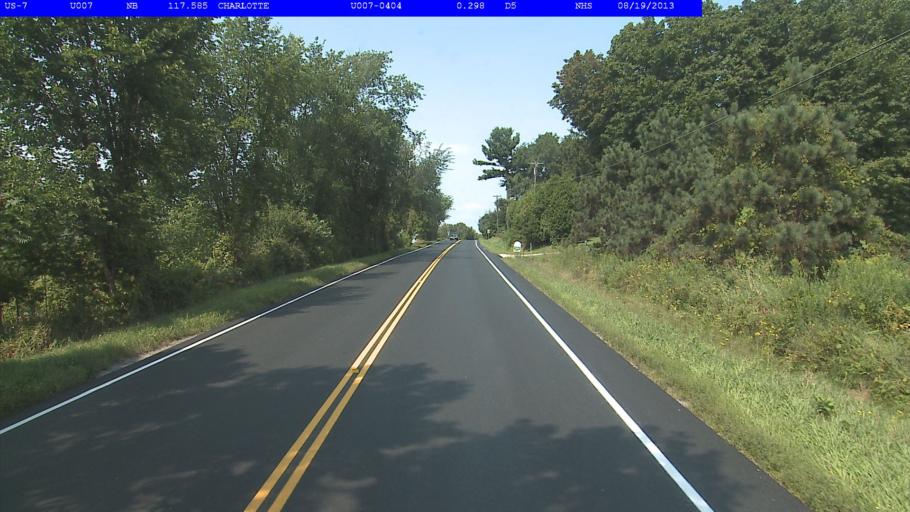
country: US
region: Vermont
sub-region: Addison County
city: Vergennes
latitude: 44.2666
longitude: -73.2325
